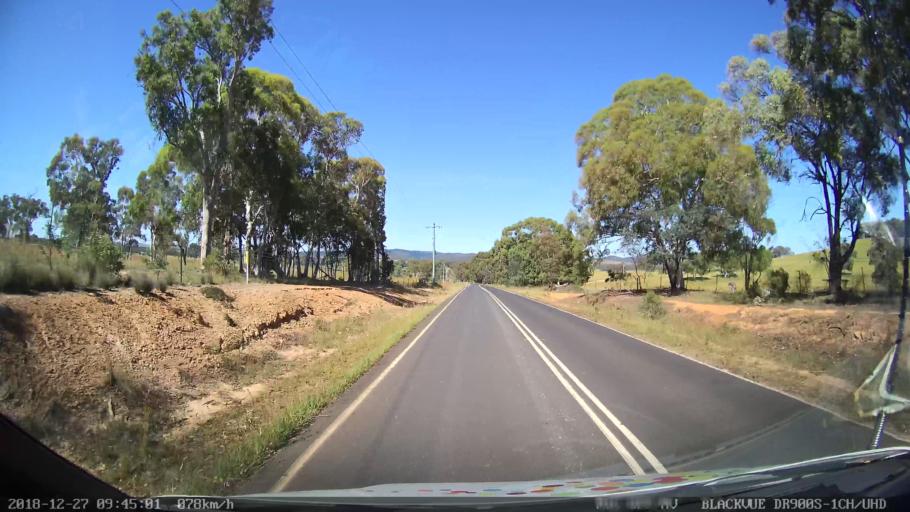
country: AU
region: New South Wales
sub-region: Lithgow
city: Portland
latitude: -33.3209
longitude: 149.9881
